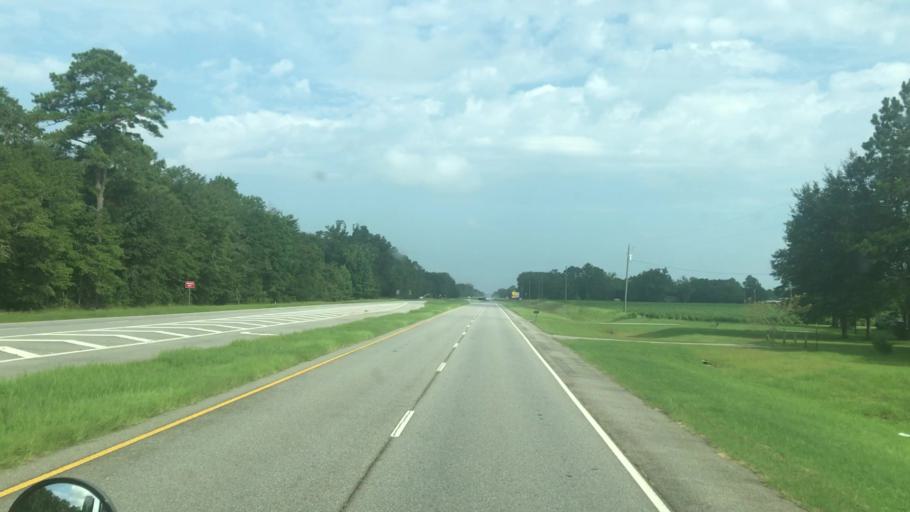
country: US
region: Georgia
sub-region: Early County
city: Blakely
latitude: 31.2764
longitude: -84.8328
